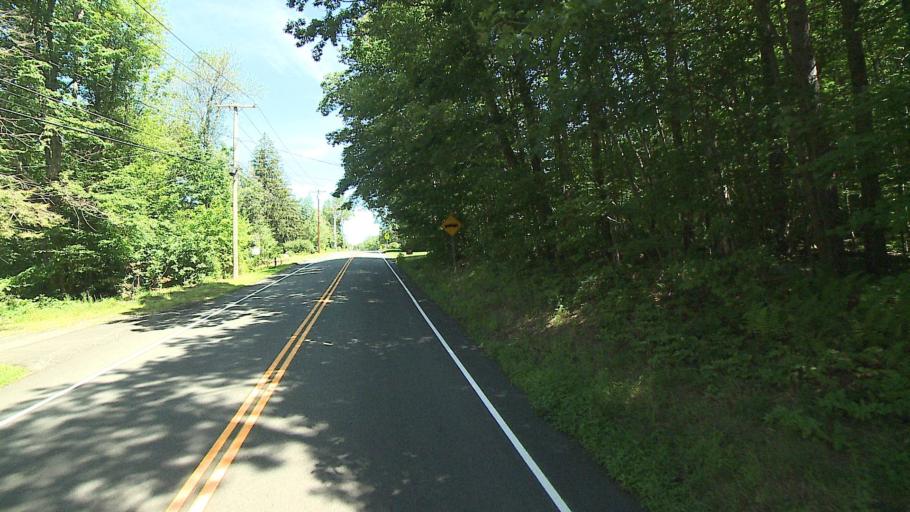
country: US
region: Connecticut
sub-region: Hartford County
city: North Granby
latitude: 41.9956
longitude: -72.9089
